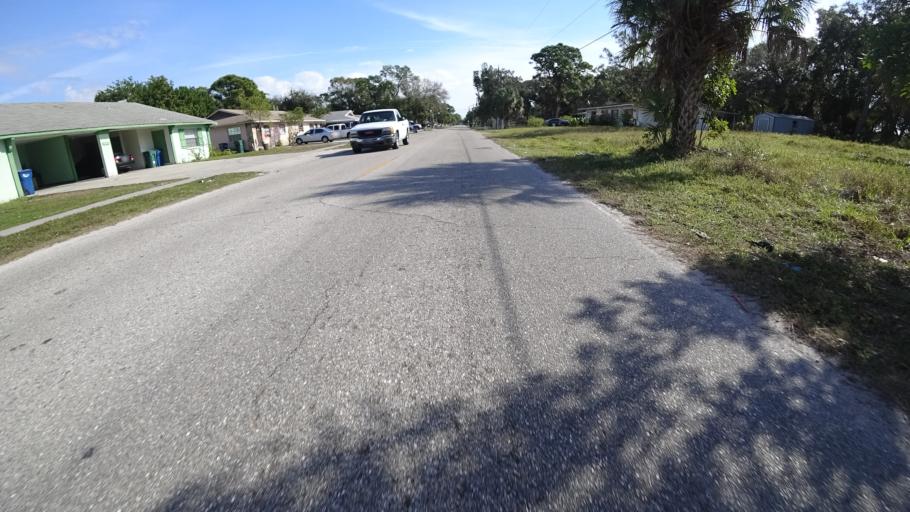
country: US
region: Florida
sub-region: Manatee County
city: Whitfield
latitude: 27.4329
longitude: -82.5621
